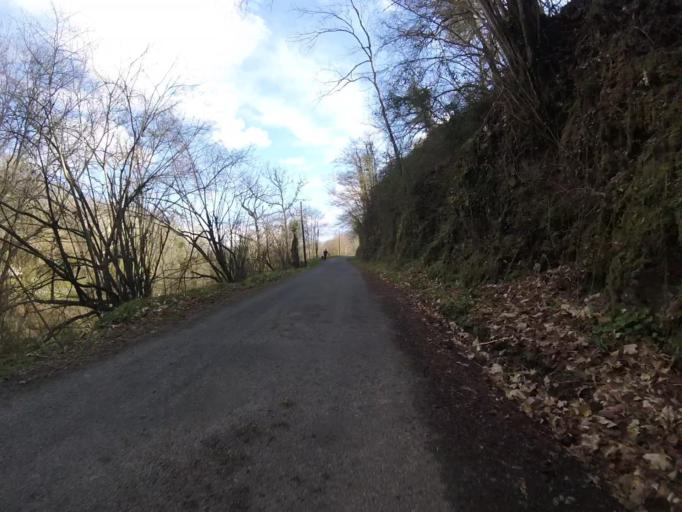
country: ES
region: Navarre
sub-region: Provincia de Navarra
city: Etxalar
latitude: 43.2684
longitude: -1.6055
